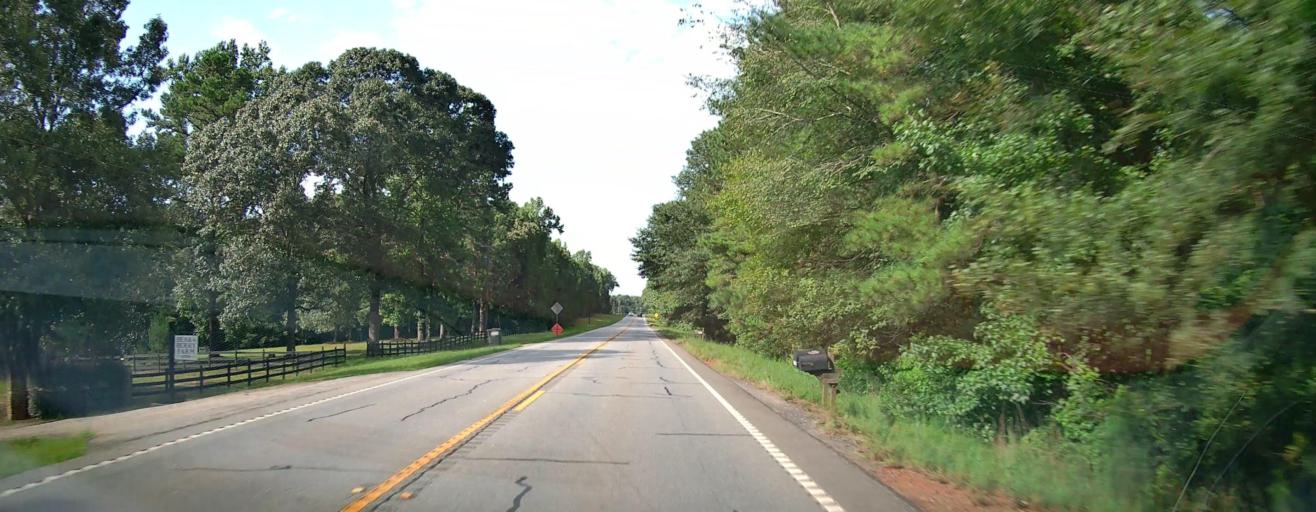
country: US
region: Georgia
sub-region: Coweta County
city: Senoia
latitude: 33.2153
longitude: -84.5791
